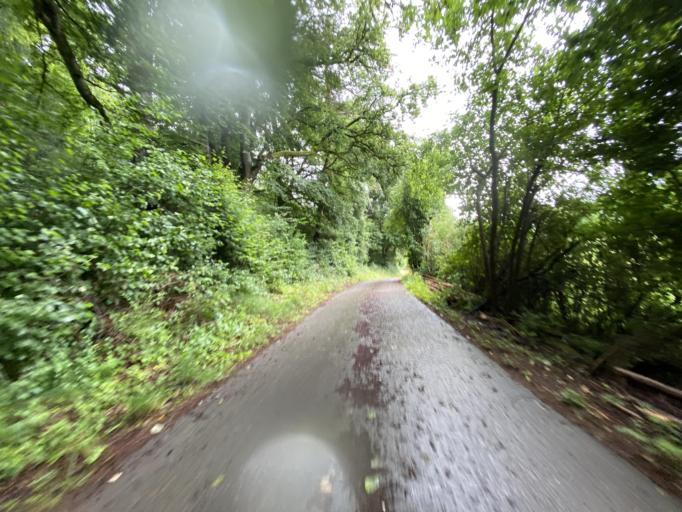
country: DE
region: Baden-Wuerttemberg
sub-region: Tuebingen Region
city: Sigmaringen
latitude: 48.1217
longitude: 9.2167
